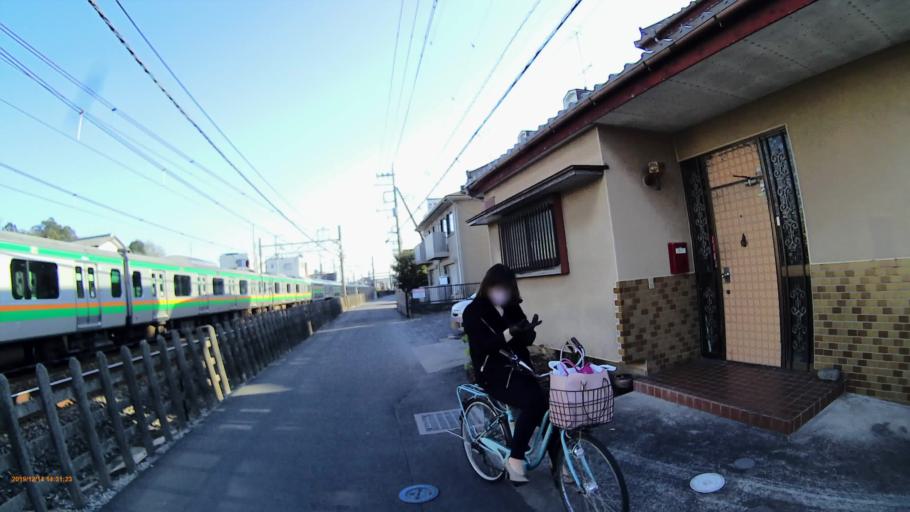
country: JP
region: Saitama
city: Konosu
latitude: 36.0363
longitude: 139.5308
